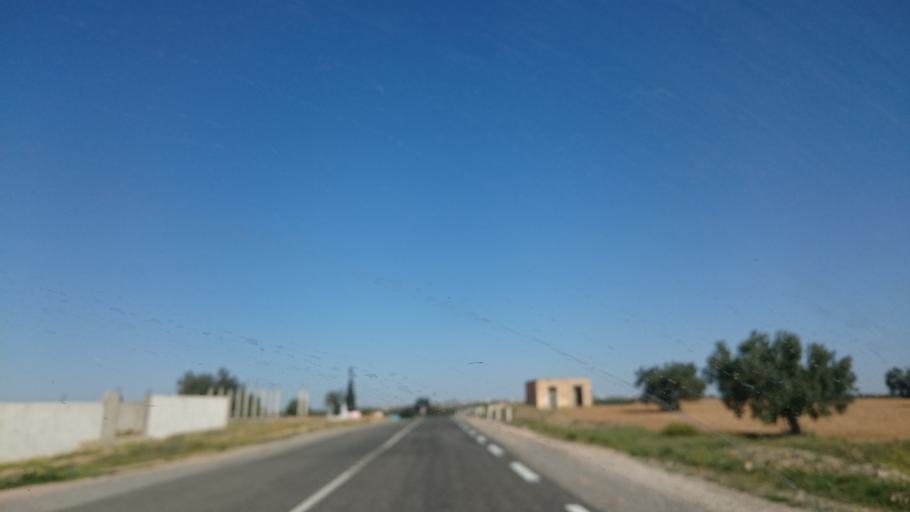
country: TN
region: Safaqis
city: Sfax
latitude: 34.7960
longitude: 10.4916
